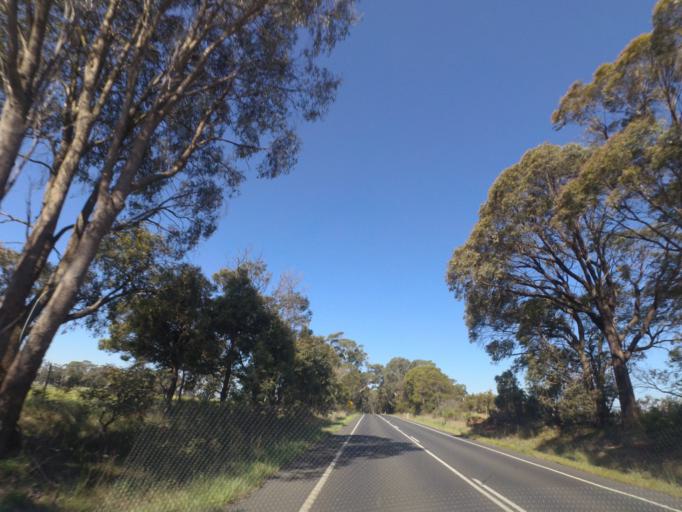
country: AU
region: Victoria
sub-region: Whittlesea
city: Whittlesea
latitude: -37.3277
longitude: 144.9789
